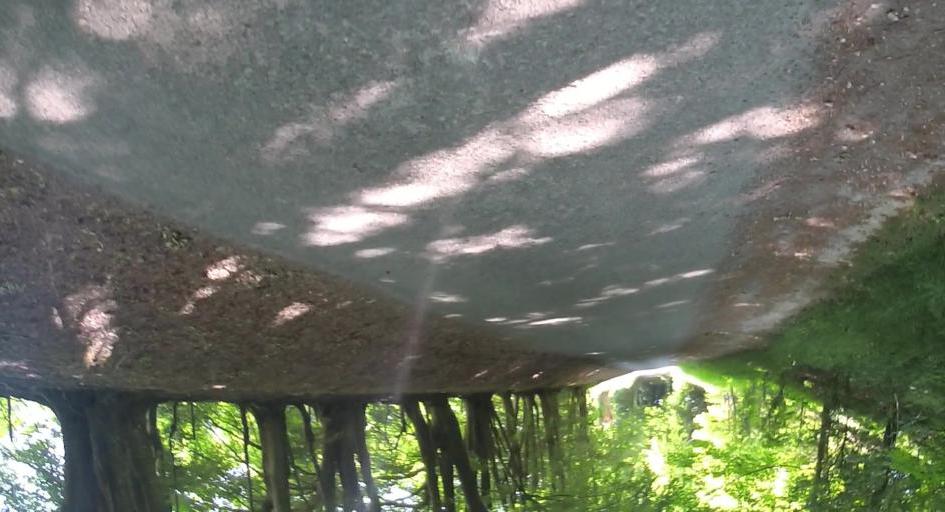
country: GB
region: England
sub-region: Hampshire
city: Kingsclere
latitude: 51.3081
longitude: -1.2960
